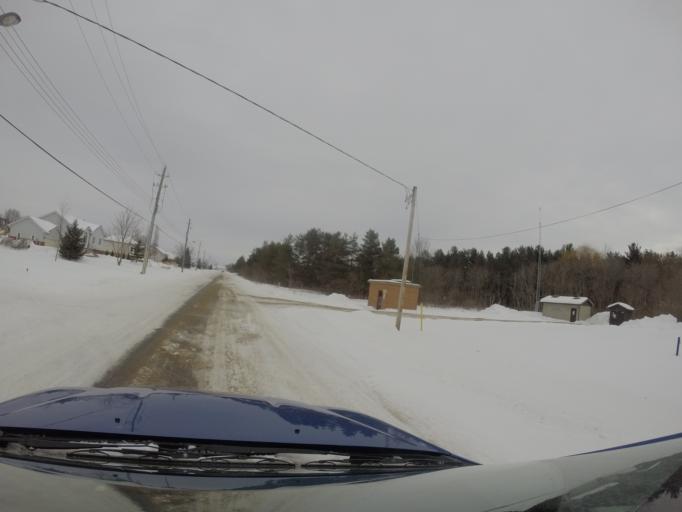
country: CA
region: Ontario
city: Wasaga Beach
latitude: 44.4214
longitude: -80.0681
